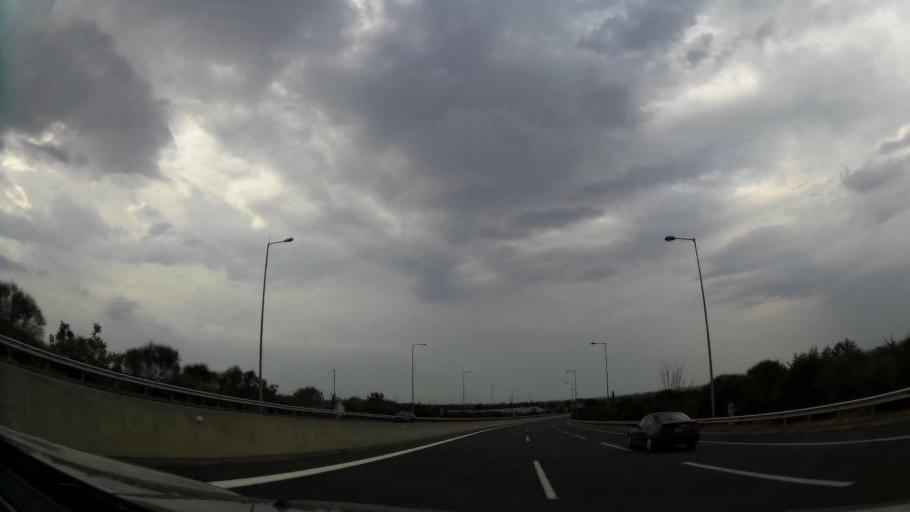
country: GR
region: Central Macedonia
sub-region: Nomos Imathias
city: Veroia
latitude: 40.5097
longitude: 22.2311
